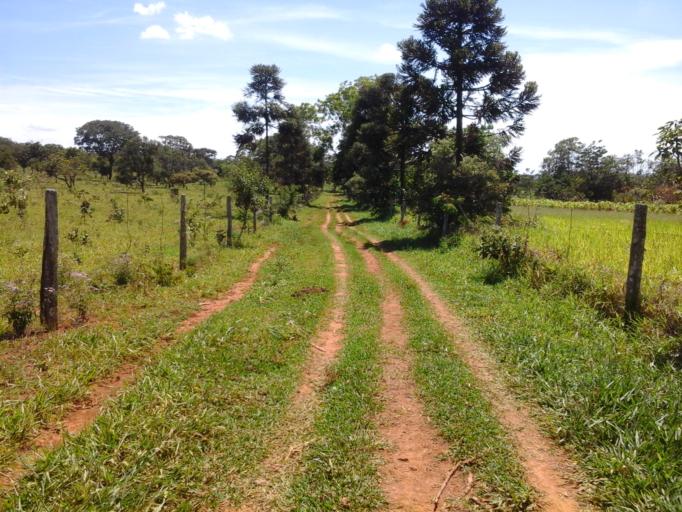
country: BR
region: Goias
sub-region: Abadiania
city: Abadiania
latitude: -15.9801
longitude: -48.5336
